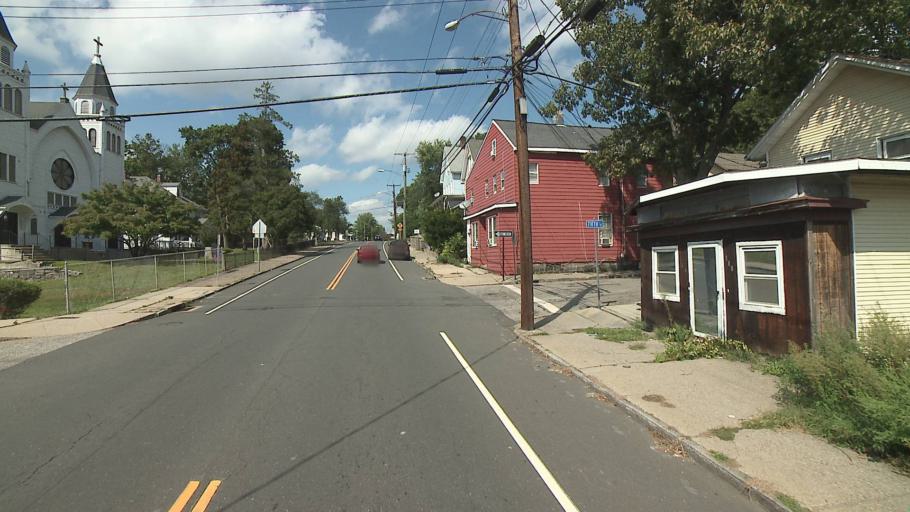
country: US
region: Connecticut
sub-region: New Haven County
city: Ansonia
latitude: 41.3533
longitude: -73.0811
